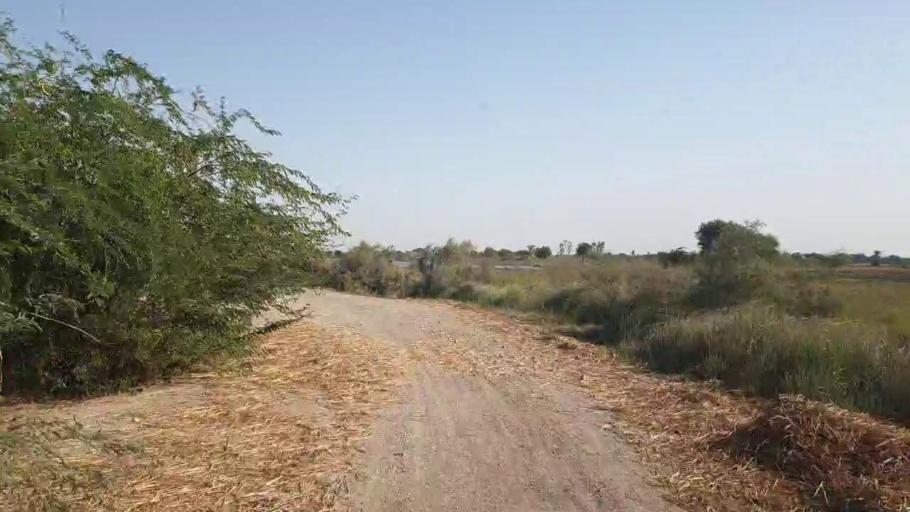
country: PK
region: Sindh
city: Matli
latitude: 25.0079
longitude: 68.7410
